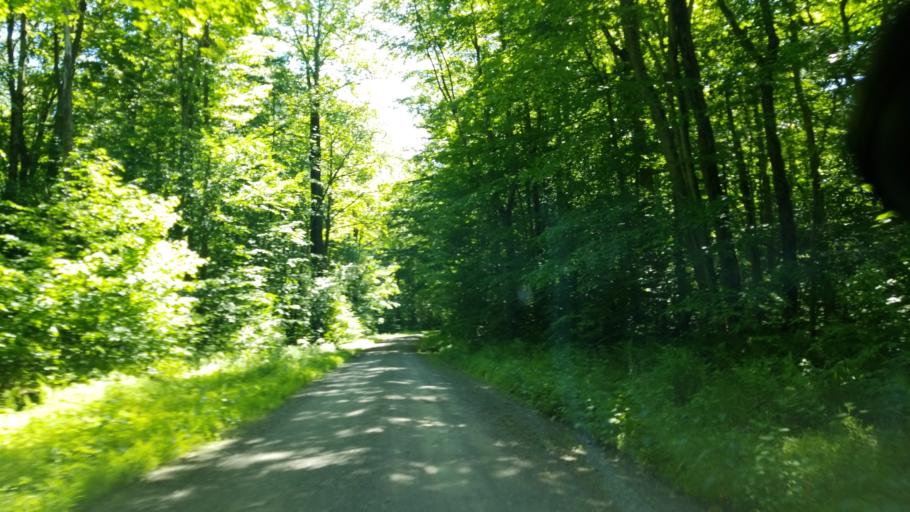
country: US
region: Pennsylvania
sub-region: Clearfield County
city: Clearfield
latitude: 41.2100
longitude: -78.4002
